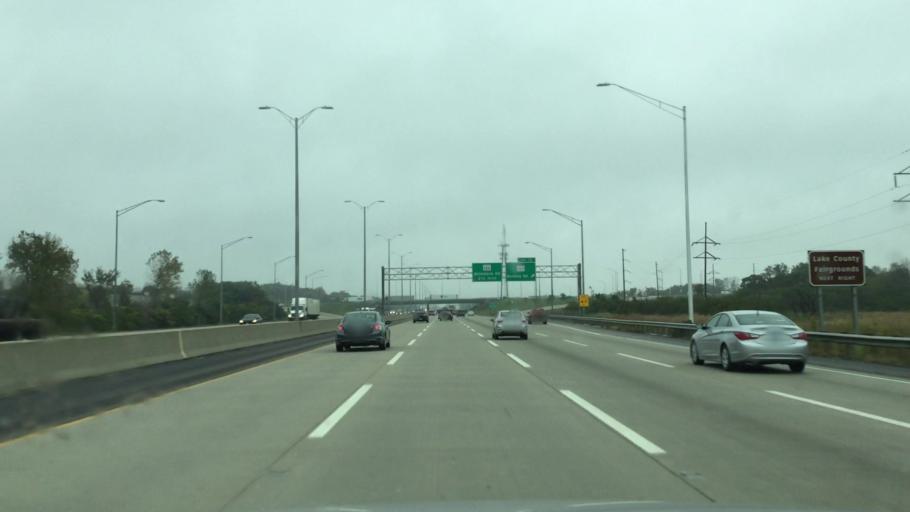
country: US
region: Illinois
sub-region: Lake County
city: Green Oaks
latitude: 42.3064
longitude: -87.9038
